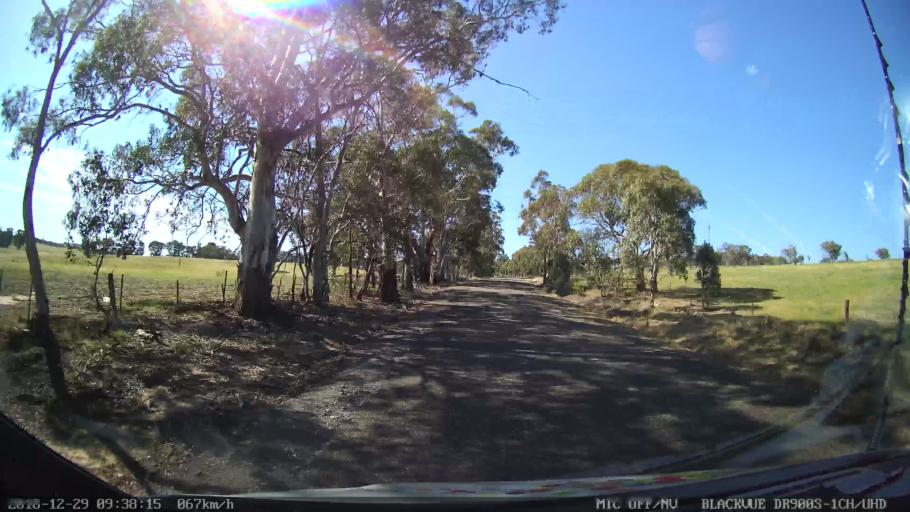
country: AU
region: New South Wales
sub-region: Upper Lachlan Shire
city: Crookwell
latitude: -34.6451
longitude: 149.3760
